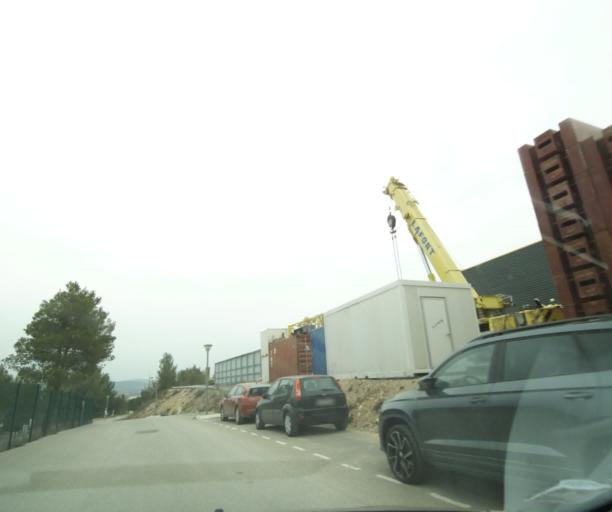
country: FR
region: Provence-Alpes-Cote d'Azur
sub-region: Departement du Vaucluse
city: Beaumont-de-Pertuis
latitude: 43.6932
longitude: 5.7346
